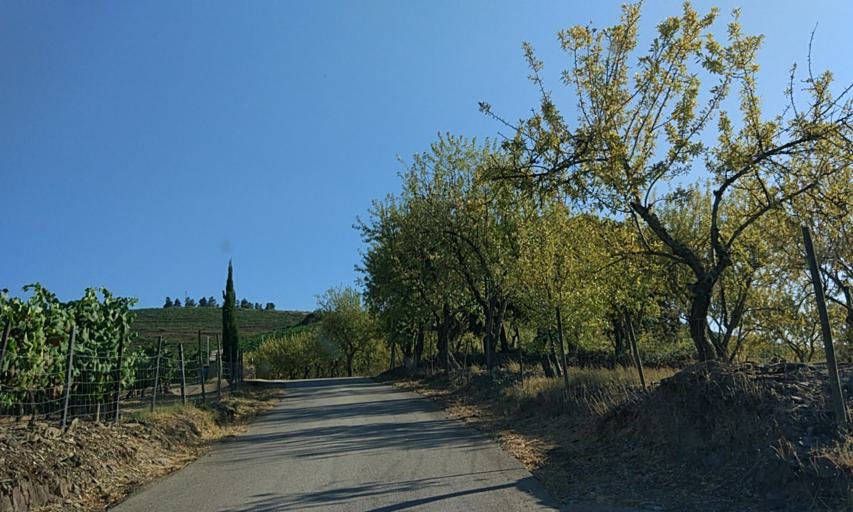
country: PT
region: Viseu
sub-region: Sao Joao da Pesqueira
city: Sao Joao da Pesqueira
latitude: 41.1724
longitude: -7.4070
